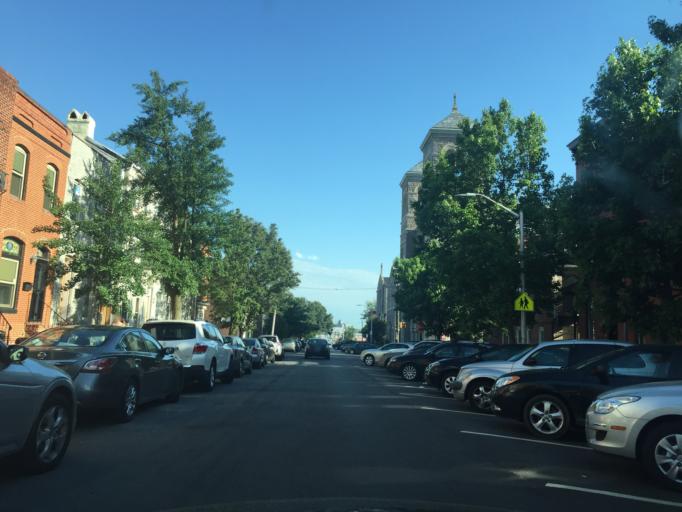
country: US
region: Maryland
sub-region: City of Baltimore
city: Baltimore
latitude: 39.2875
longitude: -76.5871
